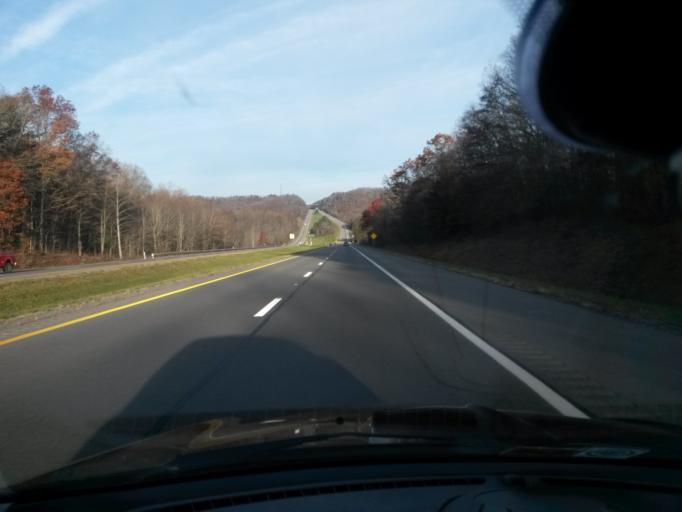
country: US
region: West Virginia
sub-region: Greenbrier County
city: Lewisburg
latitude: 37.8873
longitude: -80.5753
